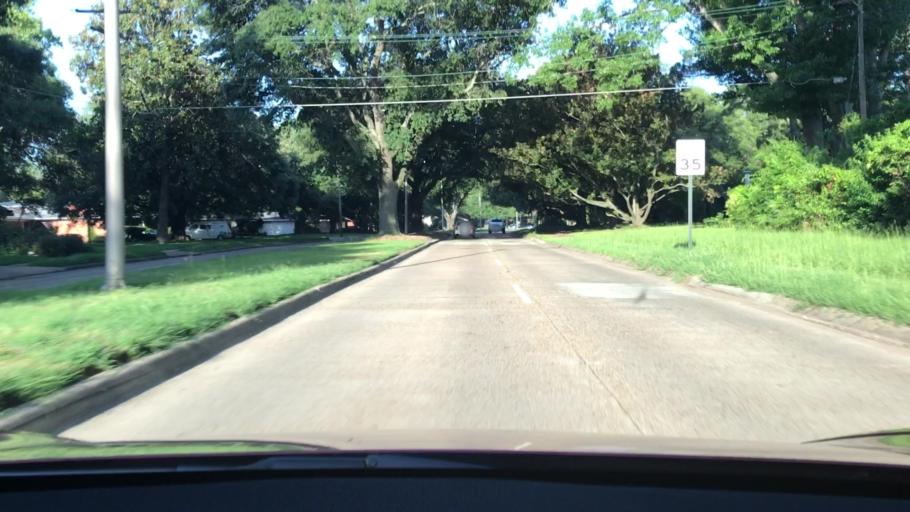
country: US
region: Louisiana
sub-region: Bossier Parish
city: Bossier City
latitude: 32.4556
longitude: -93.7306
